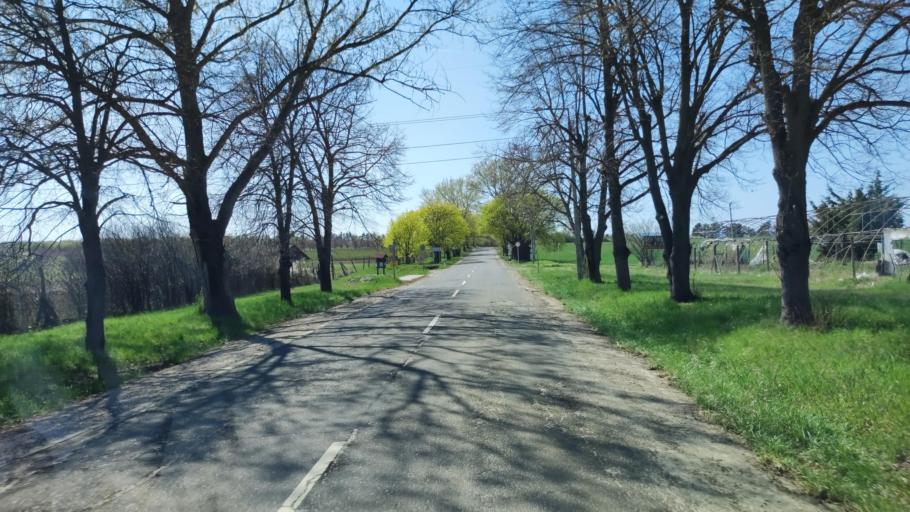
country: HU
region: Pest
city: Kosd
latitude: 47.7949
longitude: 19.1784
